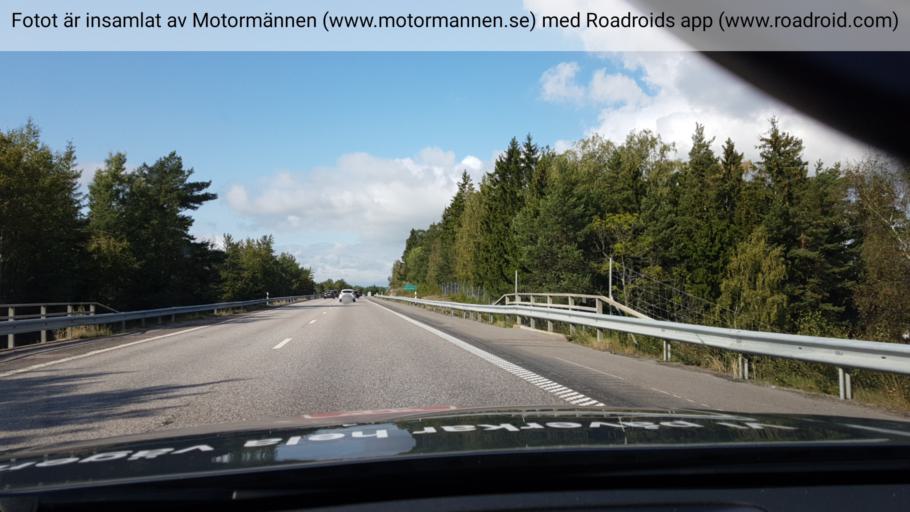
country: SE
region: Uppsala
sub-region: Knivsta Kommun
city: Knivsta
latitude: 59.7303
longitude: 17.8312
